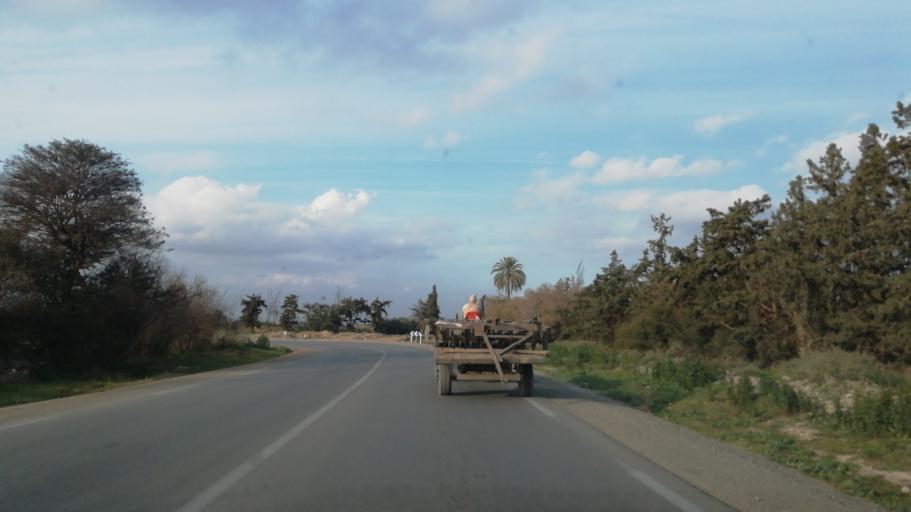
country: DZ
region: Mascara
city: Mascara
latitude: 35.6162
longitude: 0.0516
